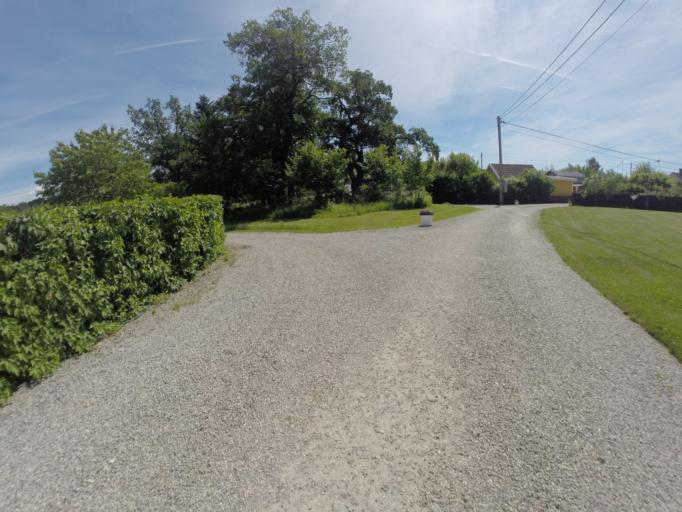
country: SE
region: Soedermanland
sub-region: Eskilstuna Kommun
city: Eskilstuna
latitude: 59.3453
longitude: 16.4960
